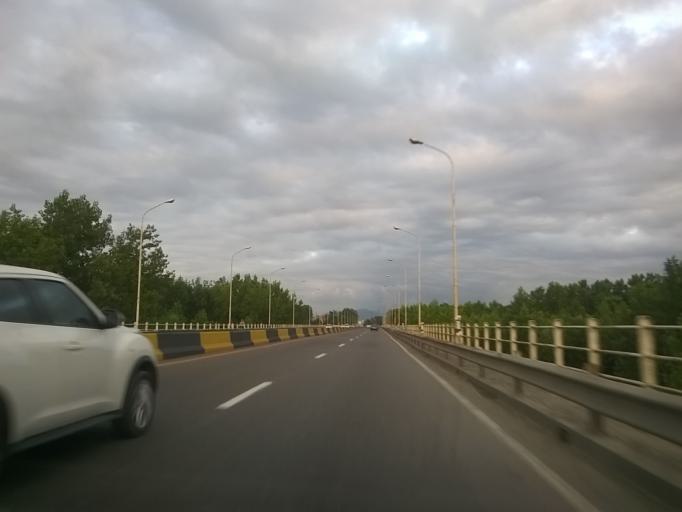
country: IR
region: Gilan
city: Astaneh-ye Ashrafiyeh
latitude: 37.2635
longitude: 49.9232
